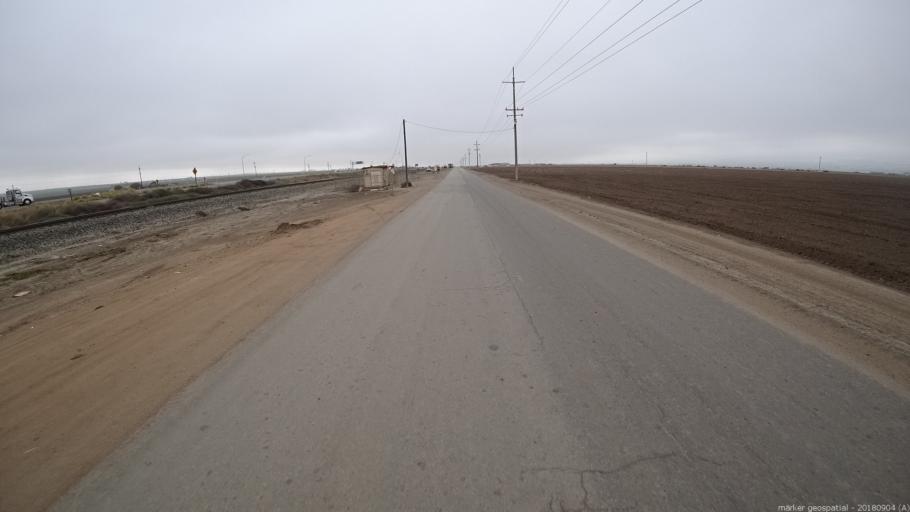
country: US
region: California
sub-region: Monterey County
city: Gonzales
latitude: 36.4903
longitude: -121.4265
